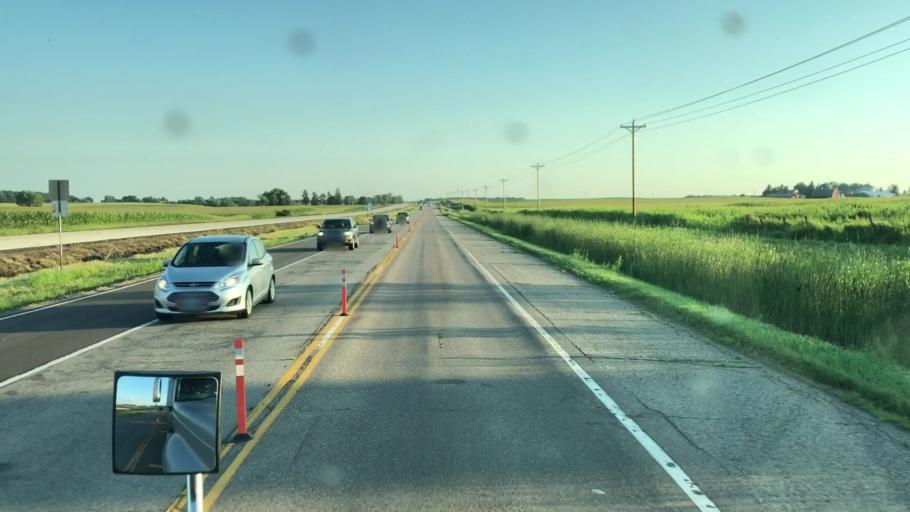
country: US
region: Minnesota
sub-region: Scott County
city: Belle Plaine
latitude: 44.5749
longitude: -93.8406
